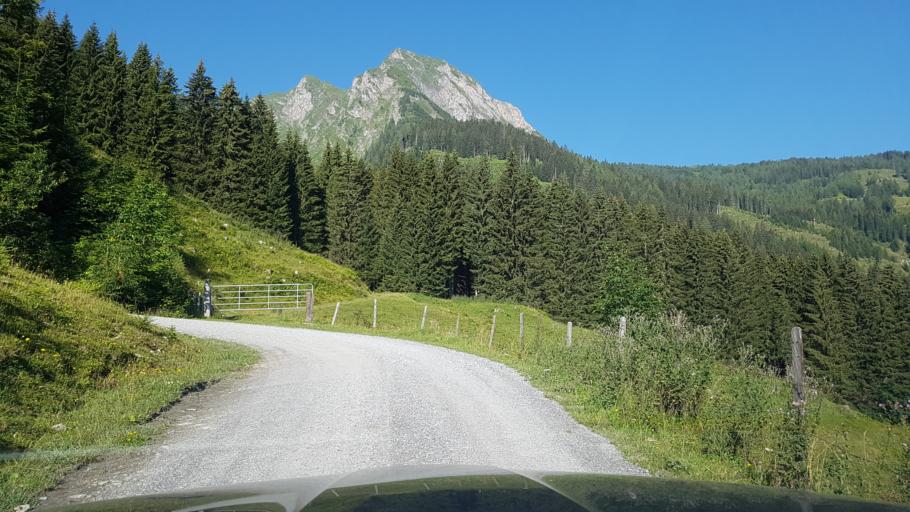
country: AT
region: Salzburg
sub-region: Politischer Bezirk Sankt Johann im Pongau
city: Dorfgastein
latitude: 47.2508
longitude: 13.0720
